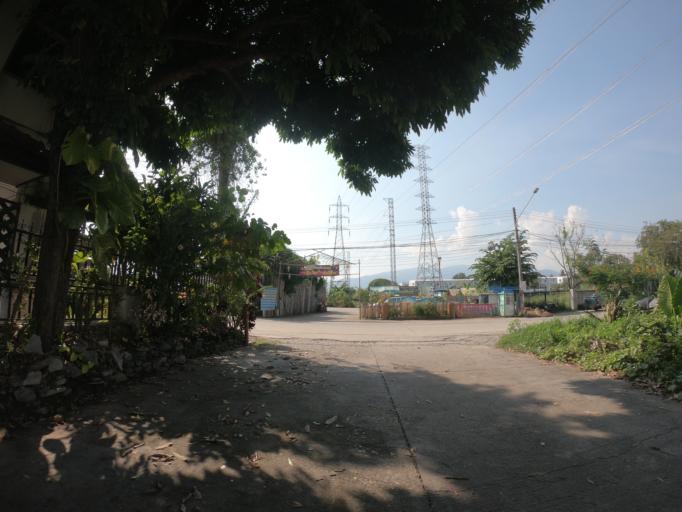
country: TH
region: Chiang Mai
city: Chiang Mai
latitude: 18.8173
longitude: 99.0072
